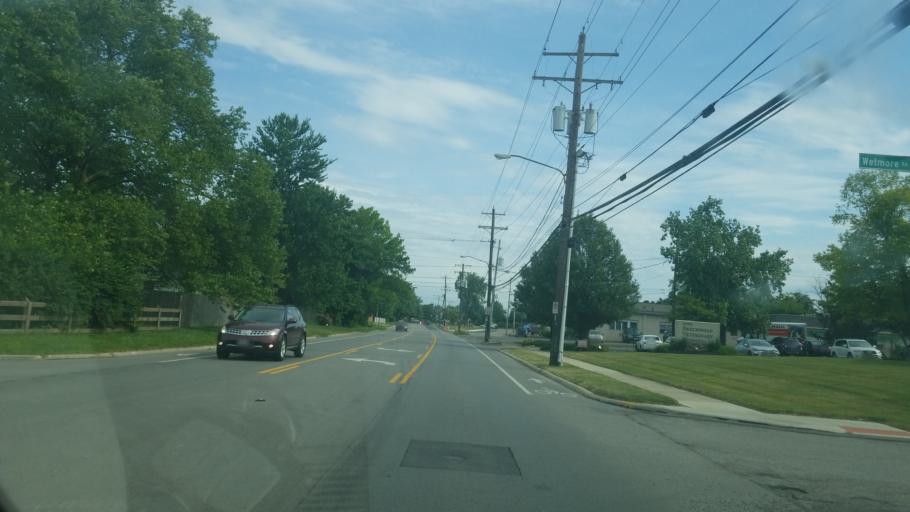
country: US
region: Ohio
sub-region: Franklin County
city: Worthington
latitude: 40.0578
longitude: -83.0006
